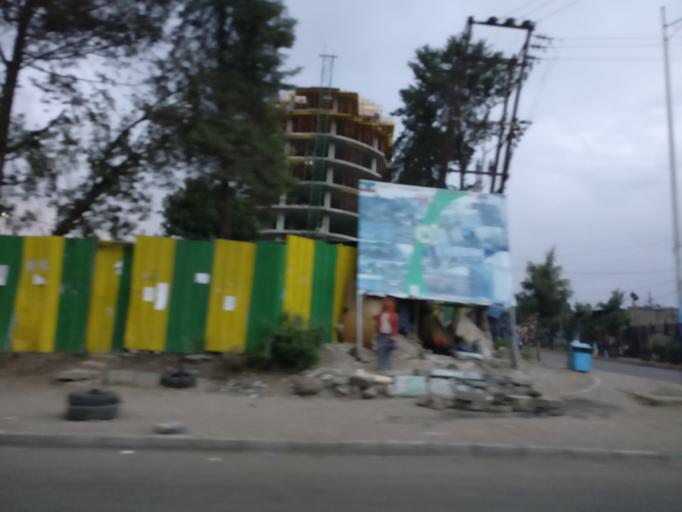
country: ET
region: Adis Abeba
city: Addis Ababa
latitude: 9.0165
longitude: 38.7379
